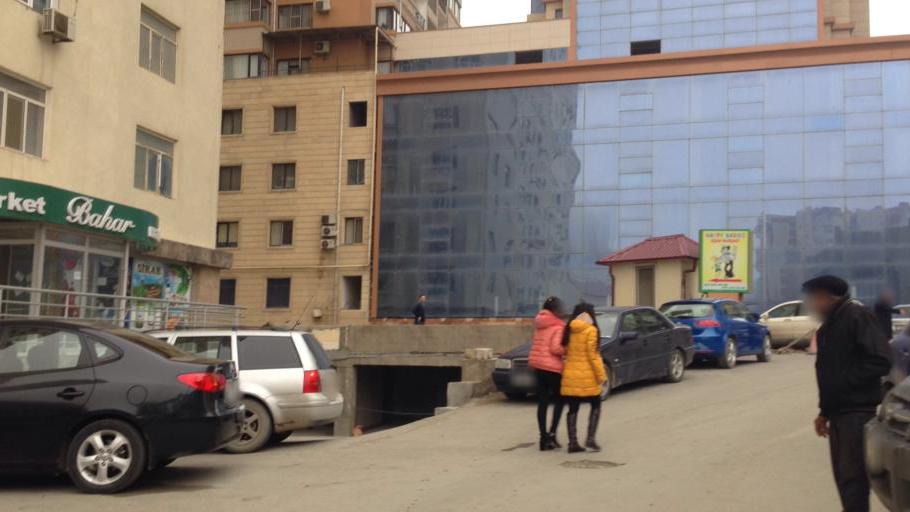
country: AZ
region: Baki
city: Baku
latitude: 40.3880
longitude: 49.8717
